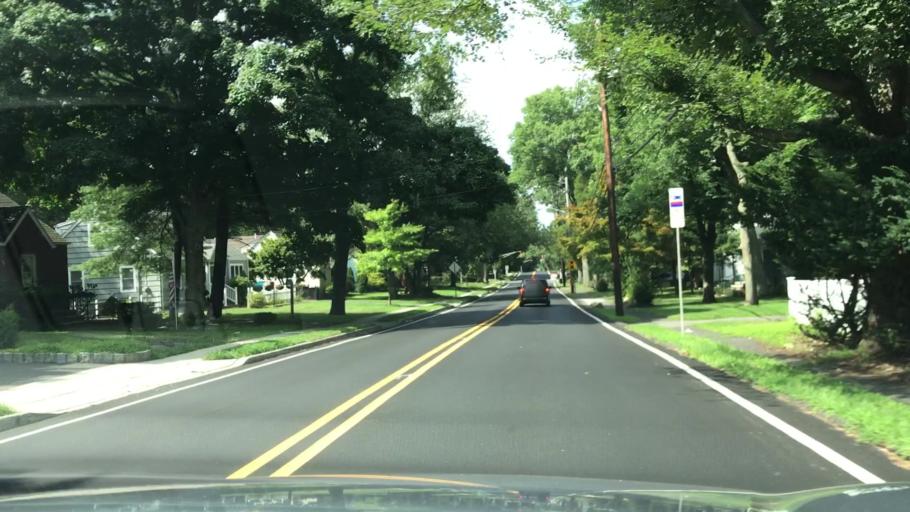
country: US
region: New Jersey
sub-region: Bergen County
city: Closter
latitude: 40.9738
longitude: -73.9733
